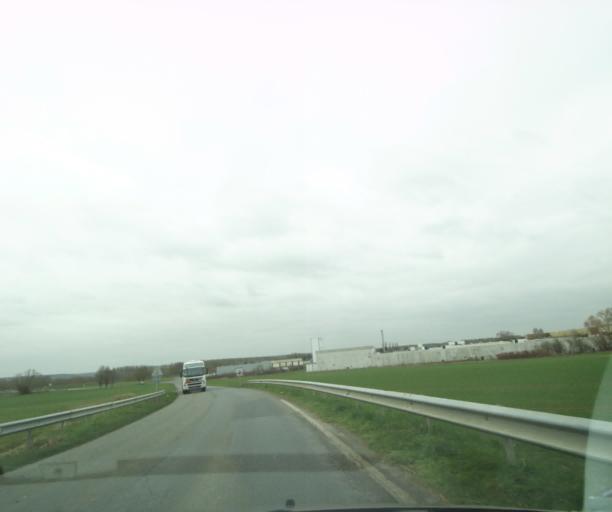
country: FR
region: Picardie
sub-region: Departement de l'Oise
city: Noyon
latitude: 49.5777
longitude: 3.0319
